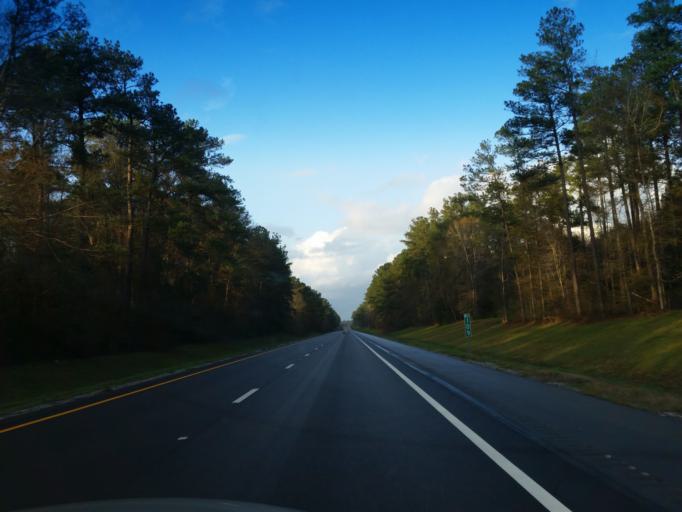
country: US
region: Mississippi
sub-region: Jones County
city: Sharon
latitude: 31.8459
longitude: -89.0486
